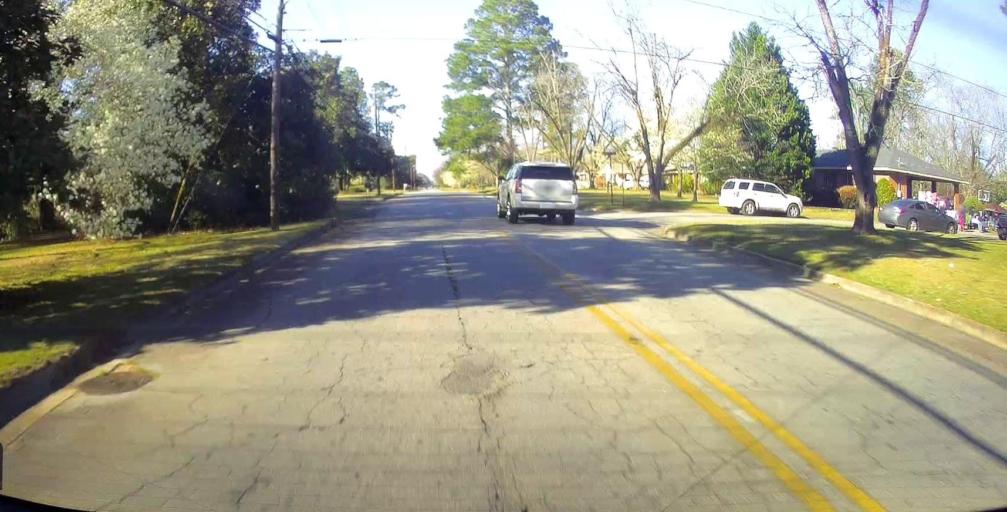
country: US
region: Georgia
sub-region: Peach County
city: Fort Valley
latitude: 32.5695
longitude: -83.8932
